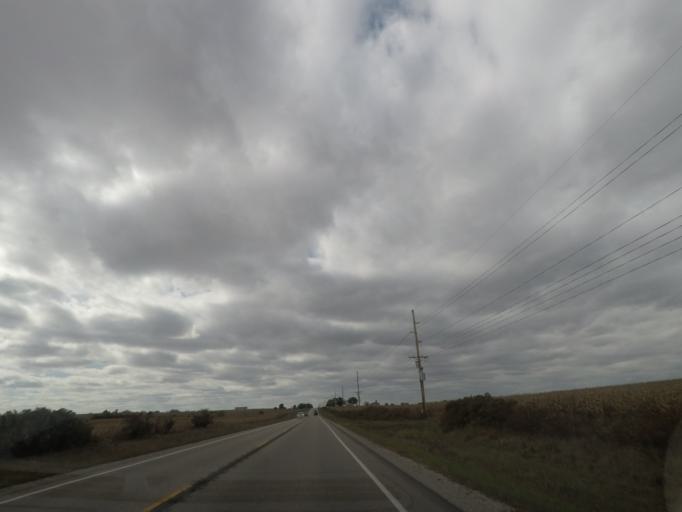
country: US
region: Iowa
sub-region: Story County
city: Huxley
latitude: 41.8777
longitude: -93.5329
